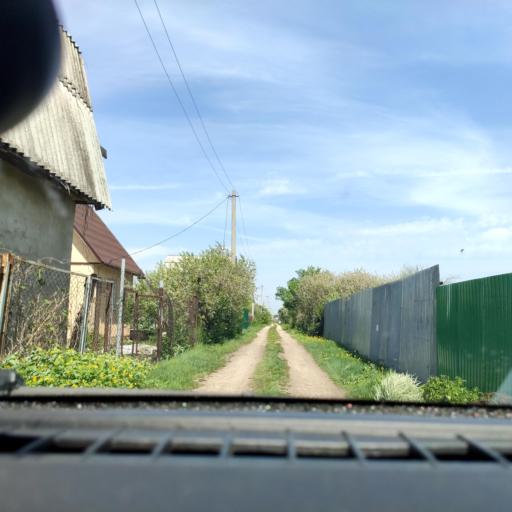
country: RU
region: Samara
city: Tol'yatti
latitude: 53.7056
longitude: 49.4126
